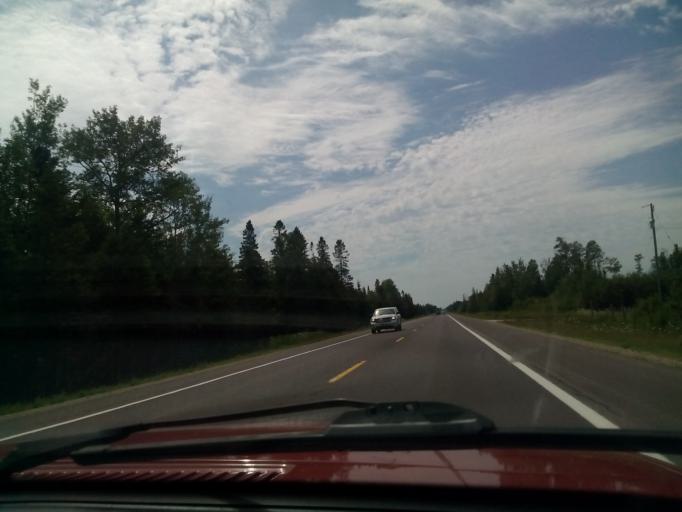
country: US
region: Michigan
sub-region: Schoolcraft County
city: Manistique
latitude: 46.0408
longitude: -85.9730
